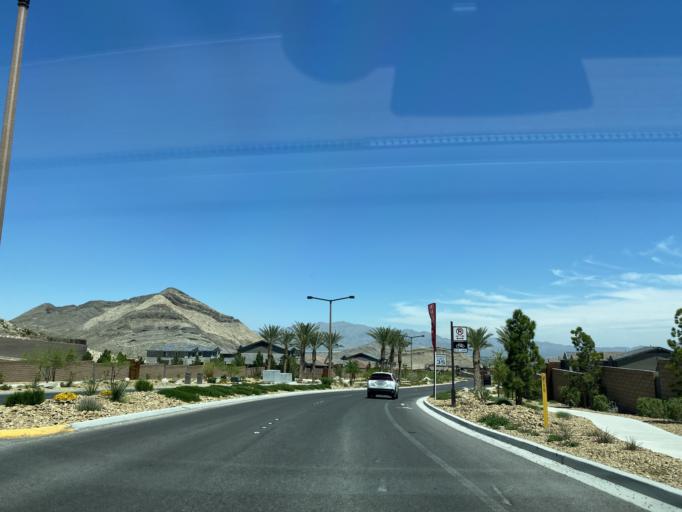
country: US
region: Nevada
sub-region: Clark County
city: Summerlin South
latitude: 36.2082
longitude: -115.3444
